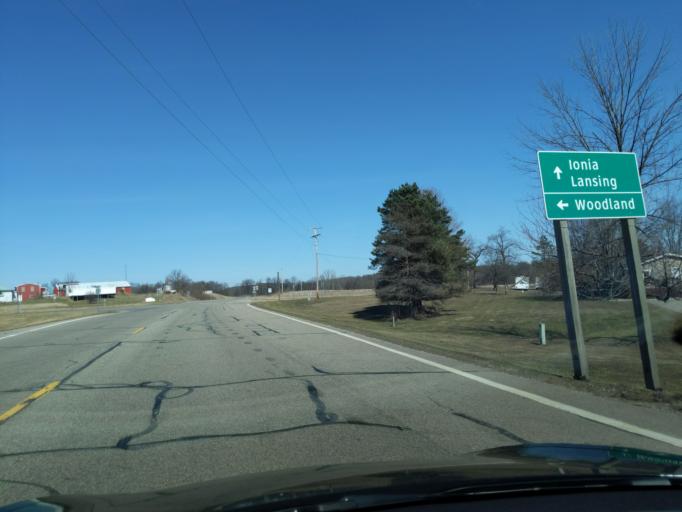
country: US
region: Michigan
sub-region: Ionia County
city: Lake Odessa
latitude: 42.7263
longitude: -85.0942
